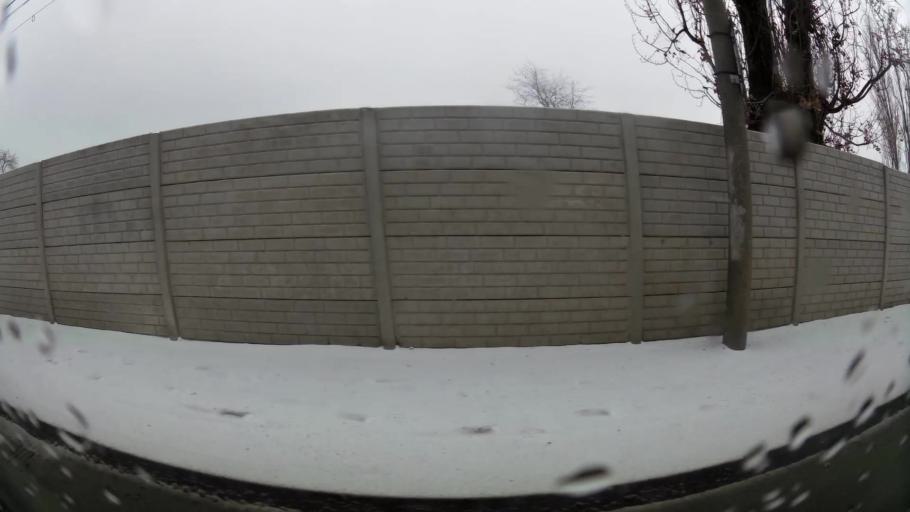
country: RO
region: Prahova
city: Ploiesti
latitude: 44.9263
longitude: 26.0060
